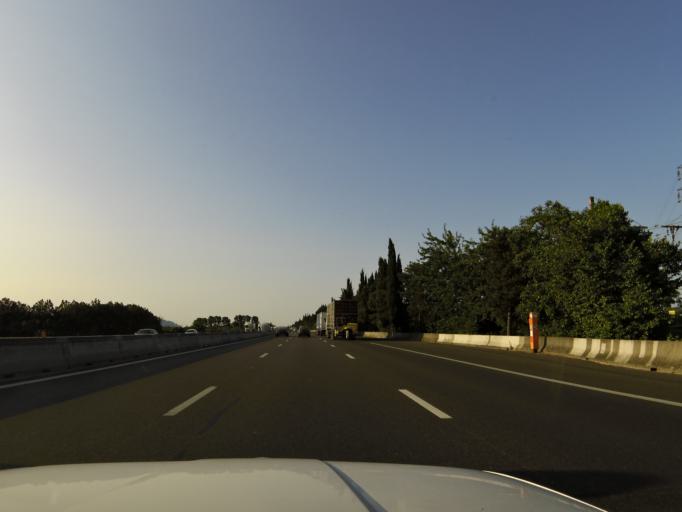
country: FR
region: Rhone-Alpes
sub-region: Departement de la Drome
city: Etoile-sur-Rhone
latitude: 44.8192
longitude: 4.8583
